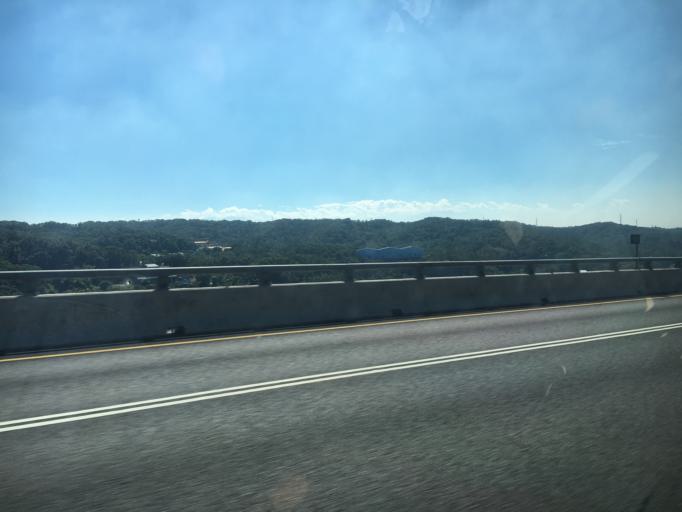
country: TW
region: Taiwan
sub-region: Taoyuan
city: Taoyuan
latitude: 25.0619
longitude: 121.3341
